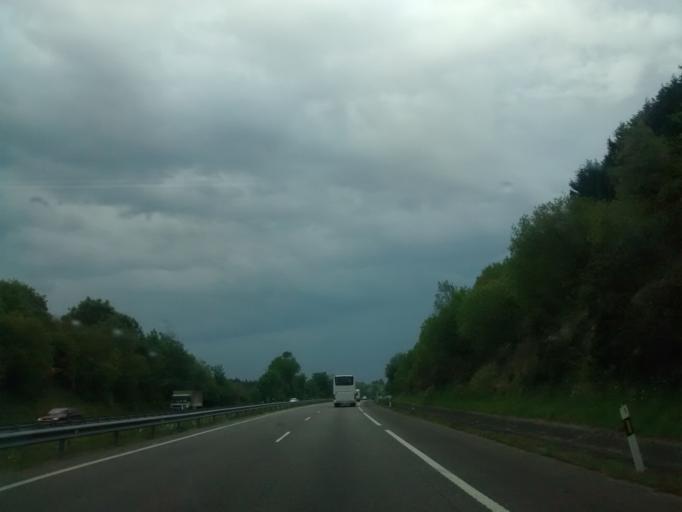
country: ES
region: Asturias
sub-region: Province of Asturias
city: Ribadesella
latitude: 43.4372
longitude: -4.9869
